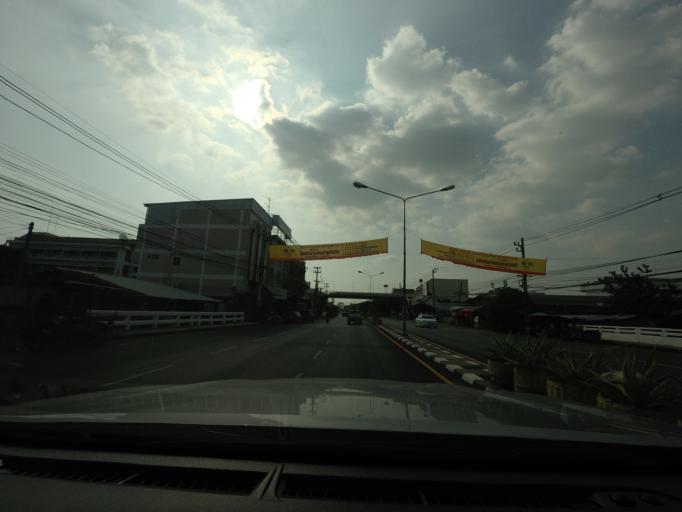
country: TH
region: Sukhothai
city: Sukhothai
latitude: 17.0087
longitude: 99.8285
